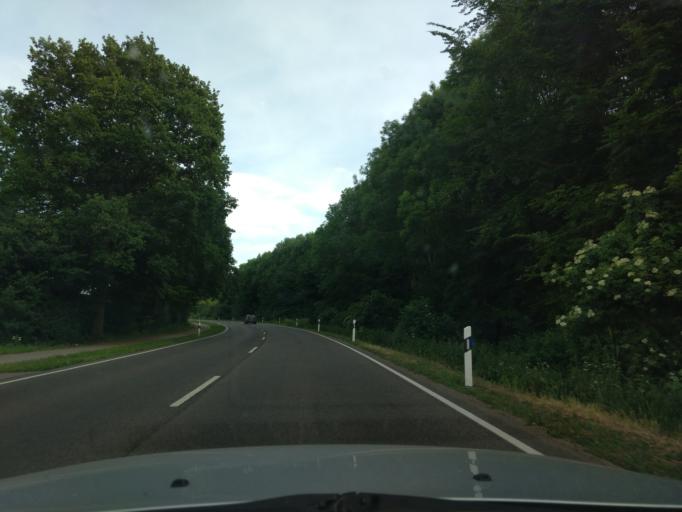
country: DE
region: North Rhine-Westphalia
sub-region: Regierungsbezirk Dusseldorf
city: Meerbusch
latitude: 51.2740
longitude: 6.6633
